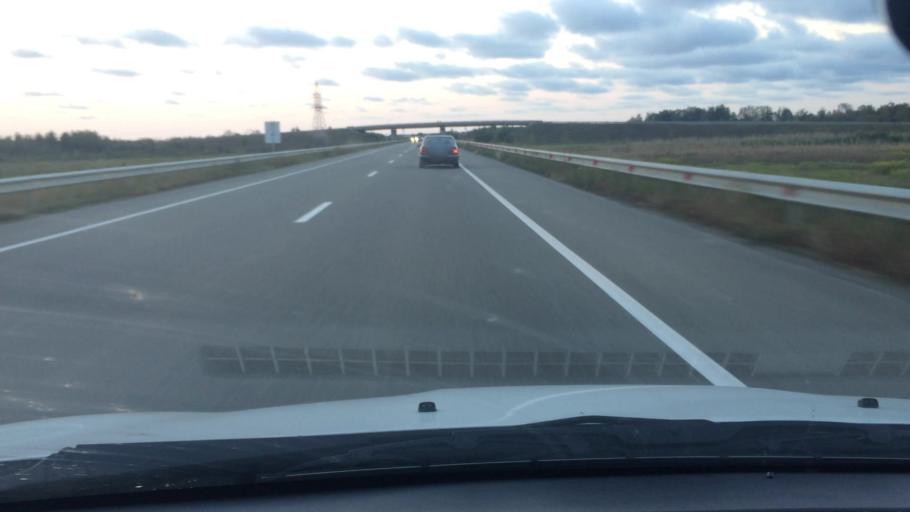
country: GE
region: Ajaria
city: Ochkhamuri
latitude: 41.8898
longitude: 41.8081
